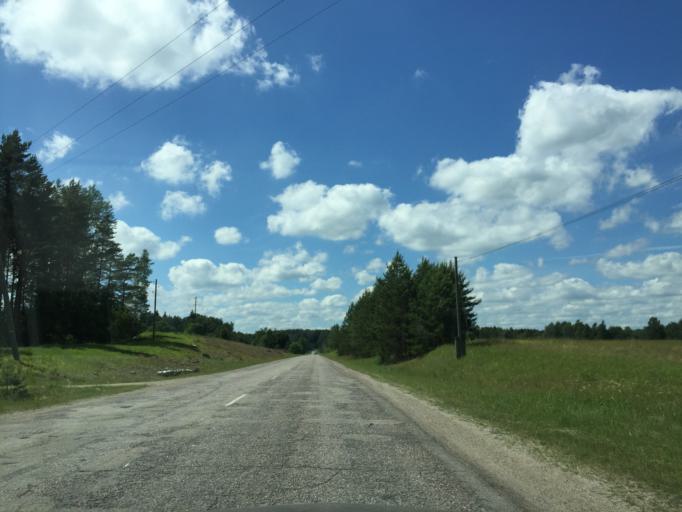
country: LV
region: Engure
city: Smarde
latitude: 56.9785
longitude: 23.3008
